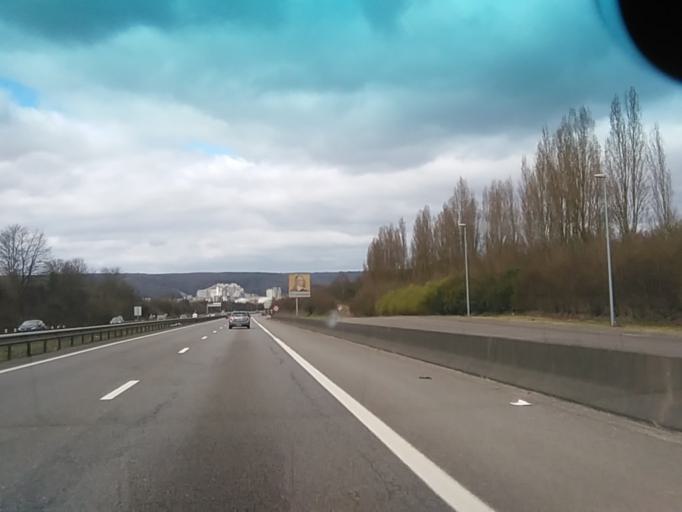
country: FR
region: Haute-Normandie
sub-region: Departement de la Seine-Maritime
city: Le Grand-Quevilly
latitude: 49.3927
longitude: 1.0388
